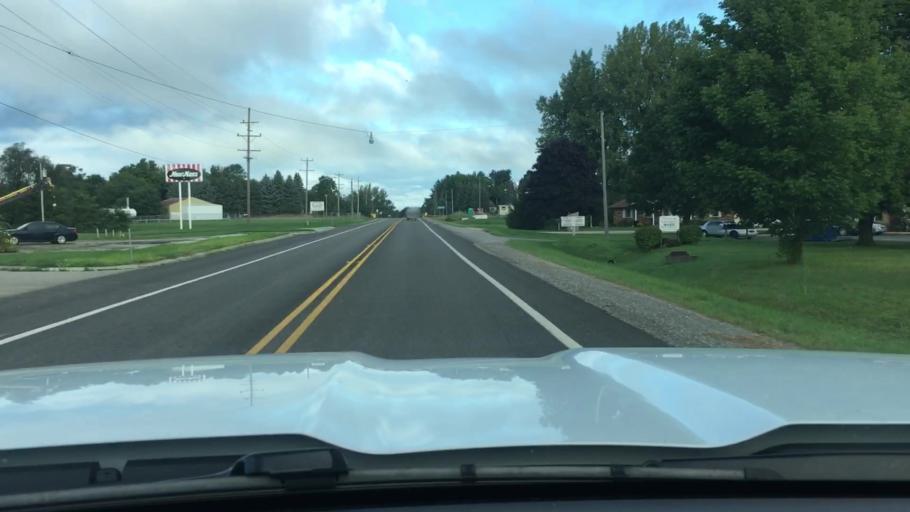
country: US
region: Michigan
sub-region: Tuscola County
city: Caro
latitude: 43.3386
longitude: -83.3487
